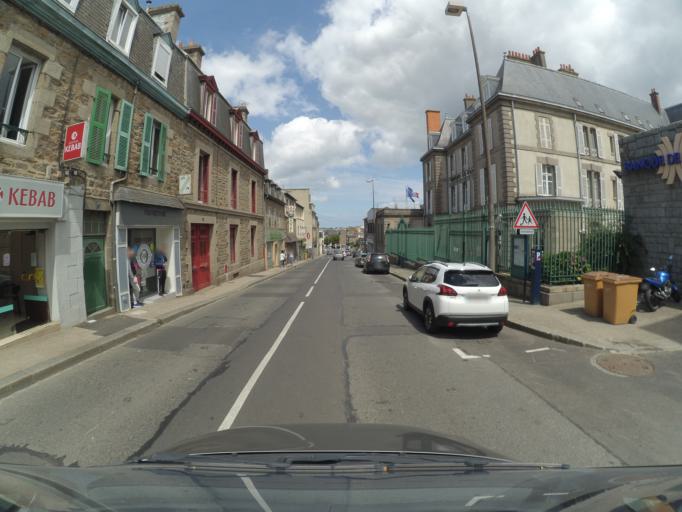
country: FR
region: Brittany
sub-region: Departement des Cotes-d'Armor
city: Saint-Brieuc
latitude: 48.5100
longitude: -2.7630
